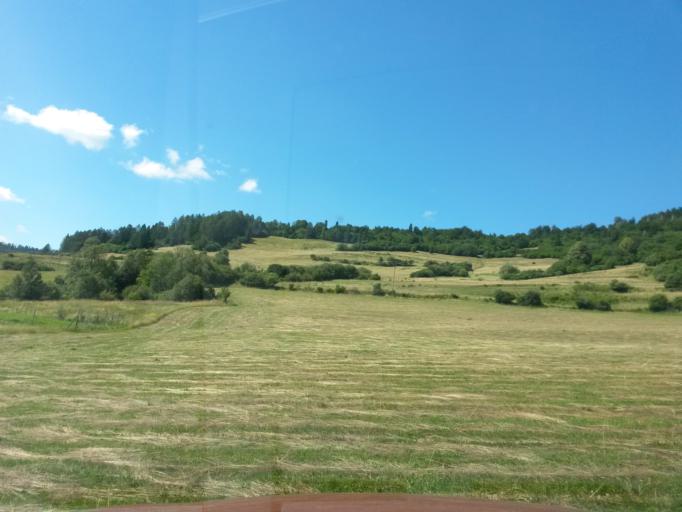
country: SK
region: Kosicky
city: Spisska Nova Ves
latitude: 48.8439
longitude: 20.6222
